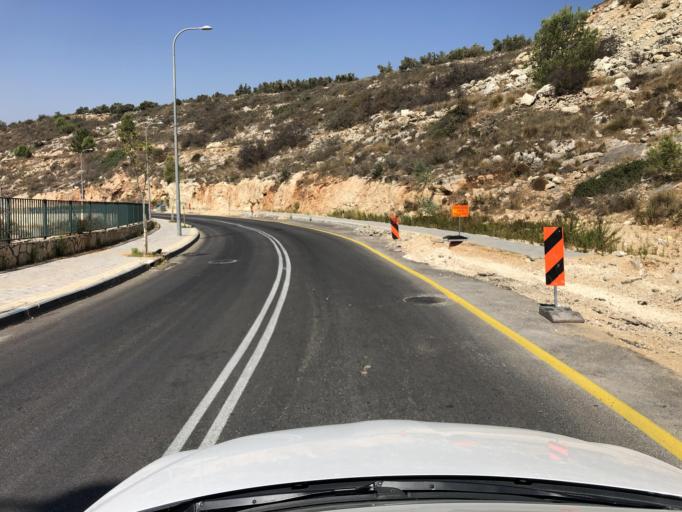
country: PS
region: West Bank
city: An Nabi Ilyas
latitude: 32.1650
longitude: 35.0167
